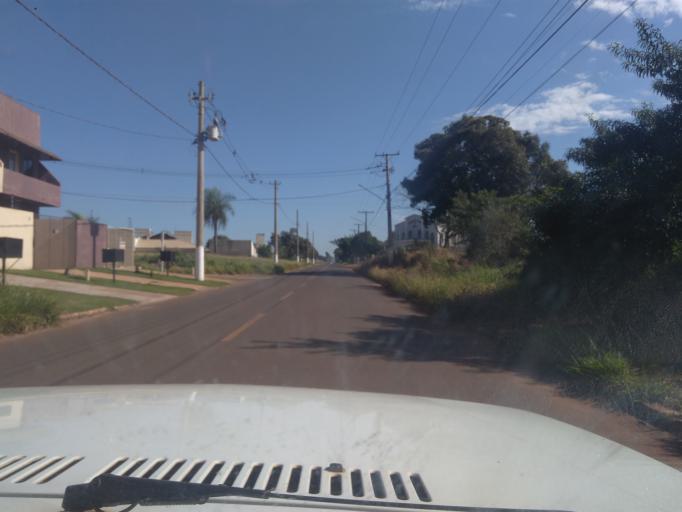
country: BR
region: Mato Grosso do Sul
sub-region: Ponta Pora
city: Ponta Pora
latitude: -22.5015
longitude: -55.7370
